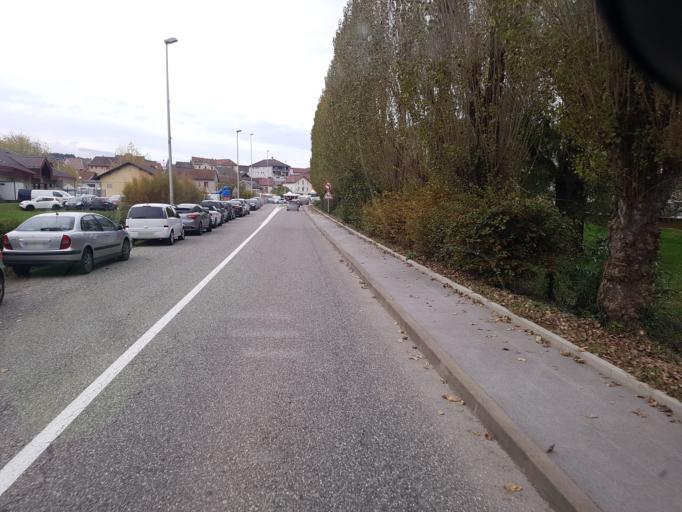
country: FR
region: Rhone-Alpes
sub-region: Departement de la Haute-Savoie
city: Versonnex
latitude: 45.9560
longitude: 5.8371
